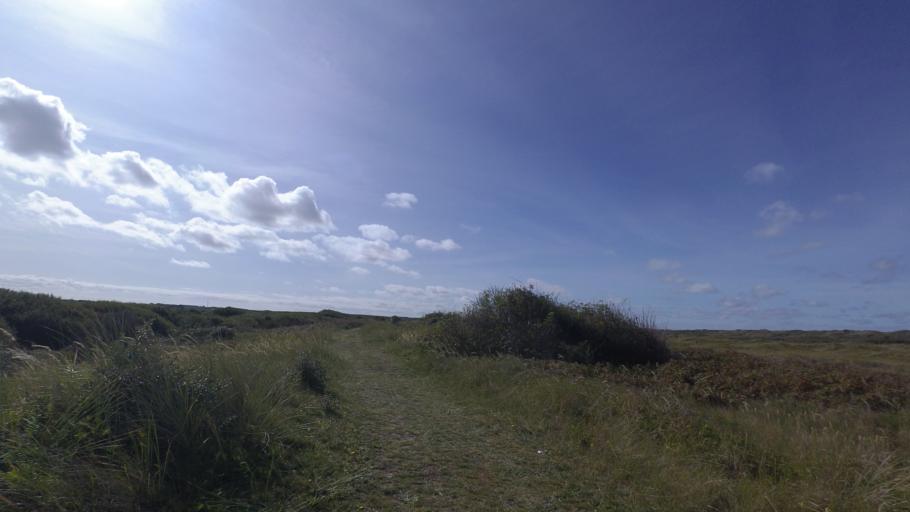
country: NL
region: Friesland
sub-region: Gemeente Ameland
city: Nes
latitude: 53.4562
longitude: 5.7412
